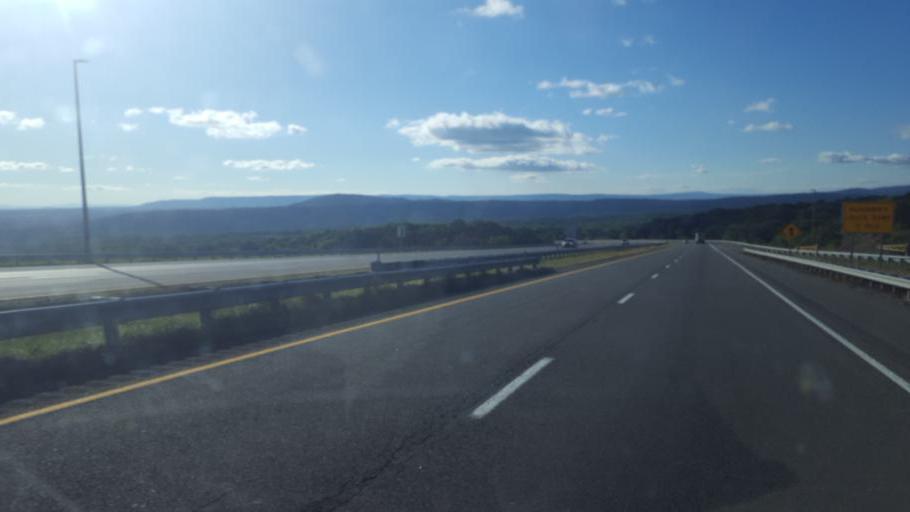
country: US
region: Maryland
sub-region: Washington County
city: Hancock
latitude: 39.7160
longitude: -78.2801
